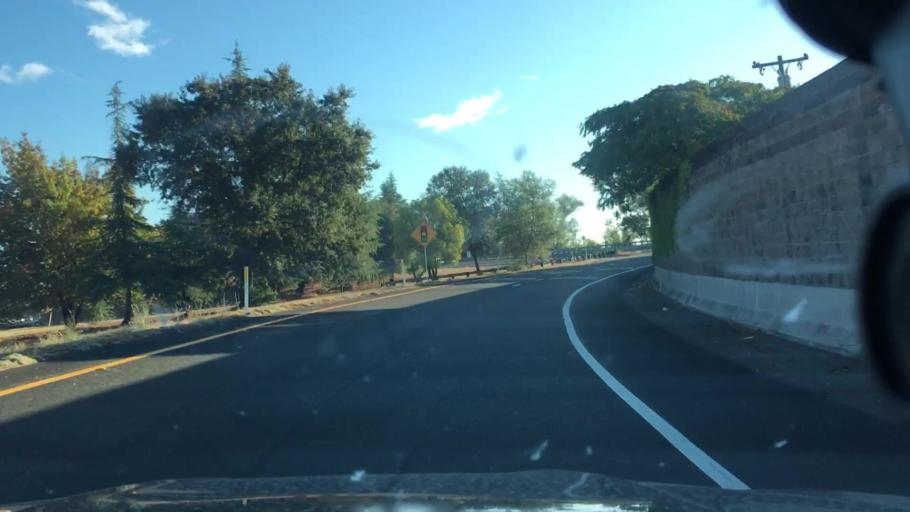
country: US
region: California
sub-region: Sacramento County
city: Antelope
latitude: 38.7061
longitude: -121.3103
